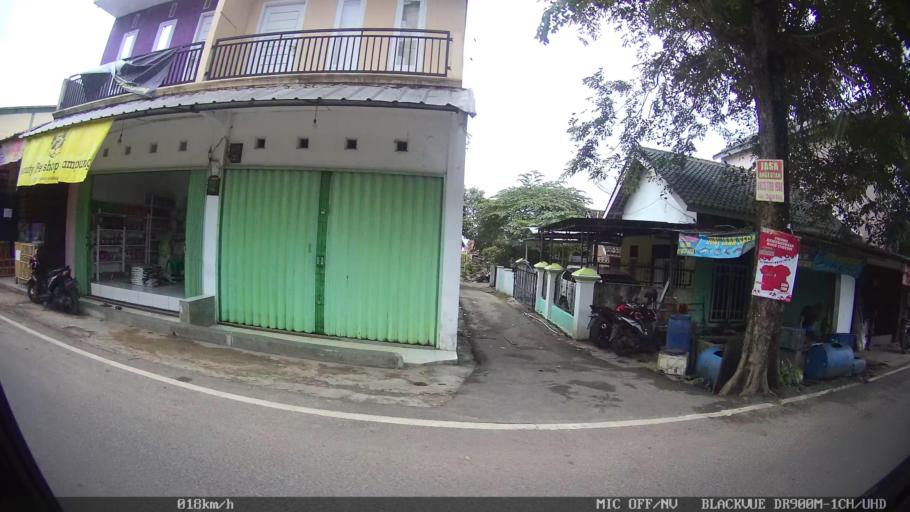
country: ID
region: Lampung
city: Kedaton
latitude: -5.3742
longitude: 105.2192
